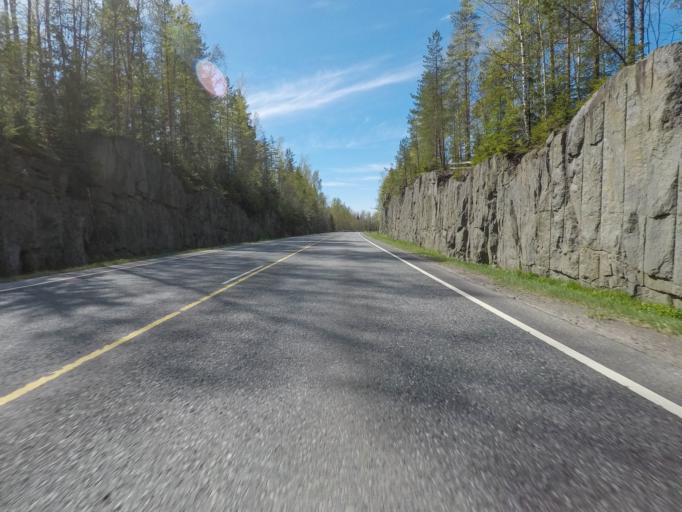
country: FI
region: Haeme
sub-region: Forssa
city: Humppila
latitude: 60.9821
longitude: 23.4411
